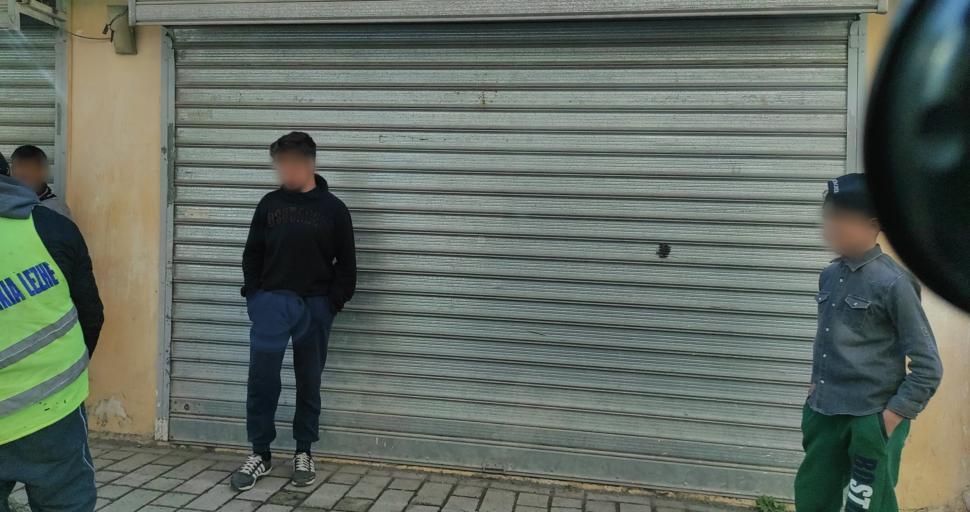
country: AL
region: Lezhe
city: Lezhe
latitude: 41.7858
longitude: 19.6440
